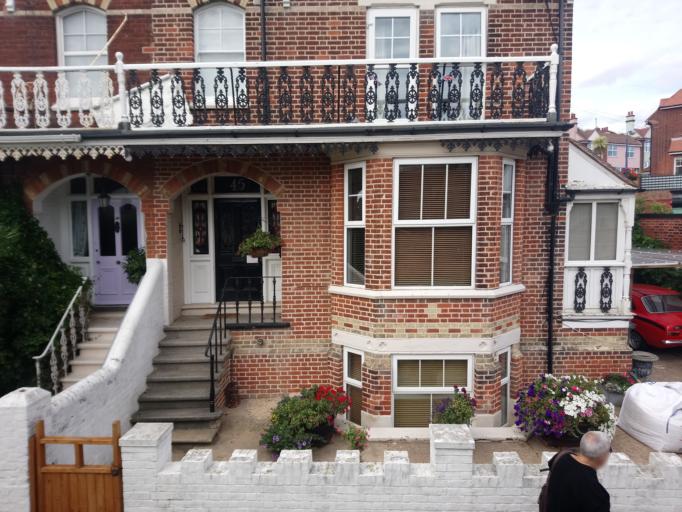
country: GB
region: England
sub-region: Suffolk
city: Felixstowe
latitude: 51.9579
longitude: 1.3452
